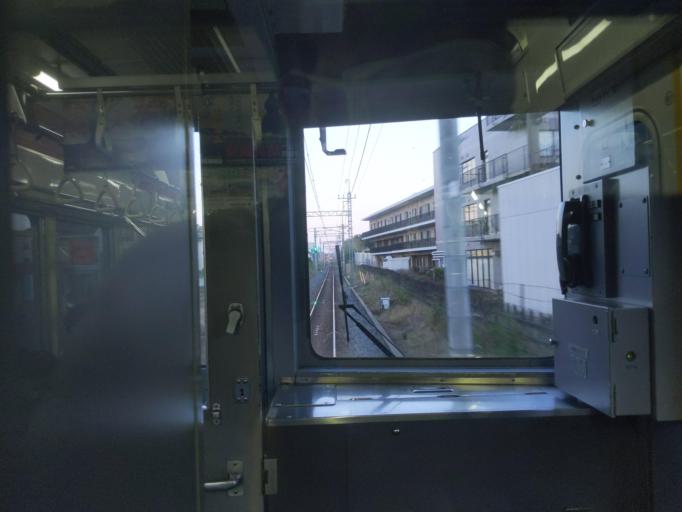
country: JP
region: Chiba
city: Noda
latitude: 35.9214
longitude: 139.9012
